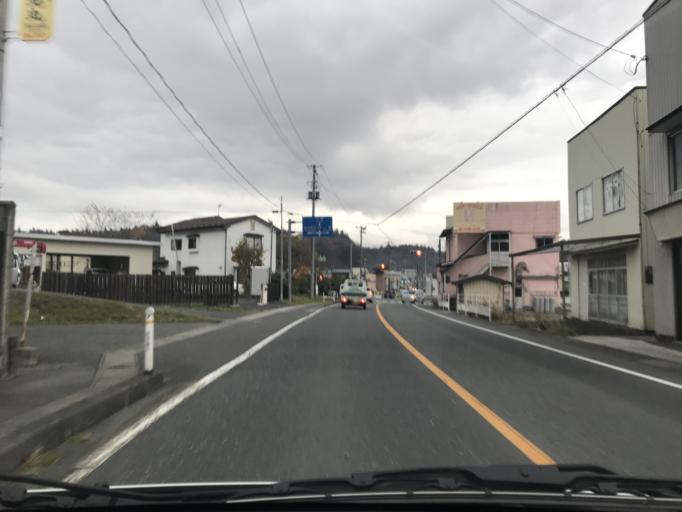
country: JP
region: Iwate
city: Ichinoseki
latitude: 38.9962
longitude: 141.3260
